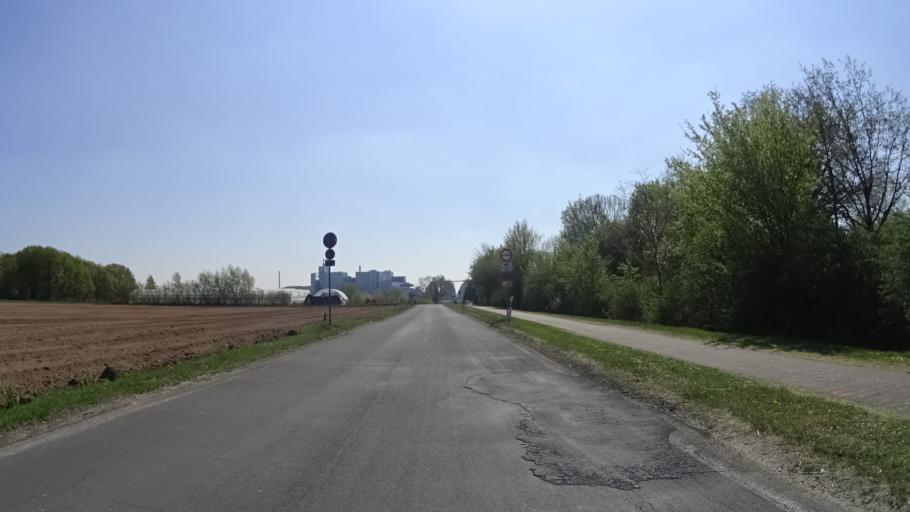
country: DE
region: North Rhine-Westphalia
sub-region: Regierungsbezirk Dusseldorf
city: Krefeld
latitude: 51.3871
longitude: 6.6312
